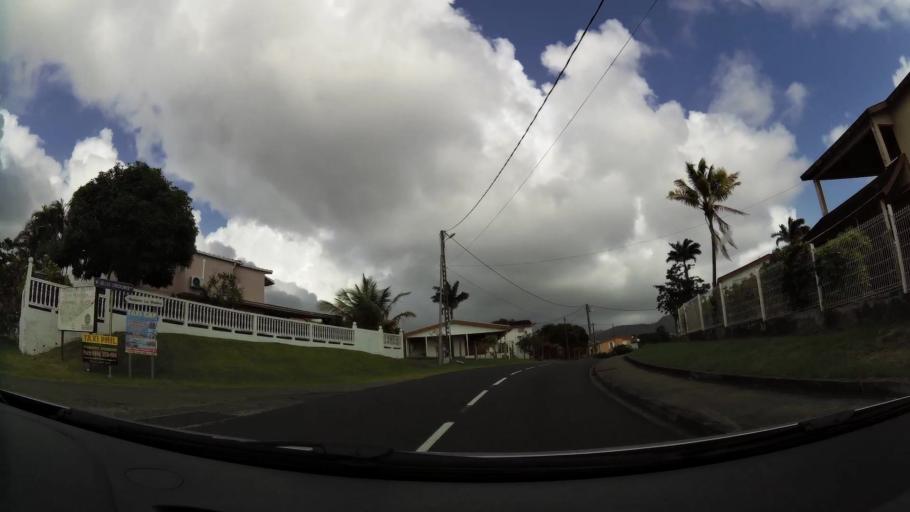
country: MQ
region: Martinique
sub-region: Martinique
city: Sainte-Luce
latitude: 14.4666
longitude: -60.9295
